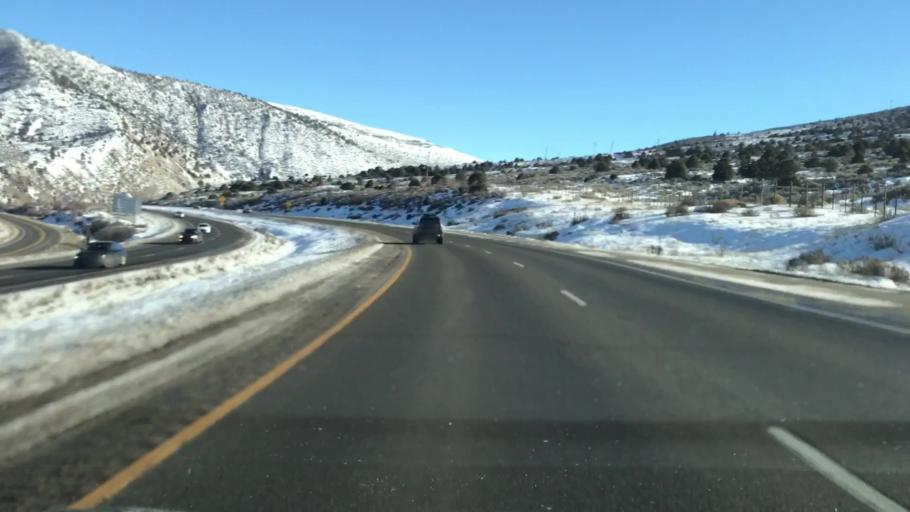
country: US
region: Colorado
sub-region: Eagle County
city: Edwards
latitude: 39.6837
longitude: -106.6592
